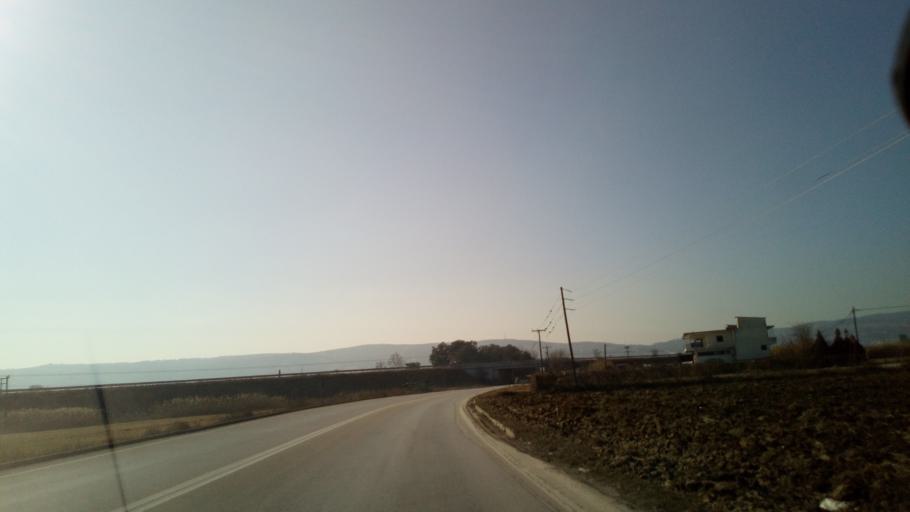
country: GR
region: Central Macedonia
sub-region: Nomos Thessalonikis
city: Kavallari
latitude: 40.7368
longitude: 23.0381
